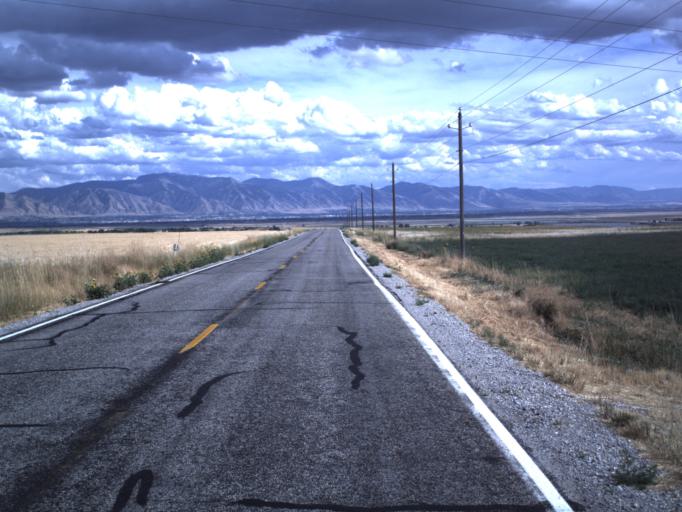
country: US
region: Utah
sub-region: Cache County
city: Benson
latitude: 41.8796
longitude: -112.0255
